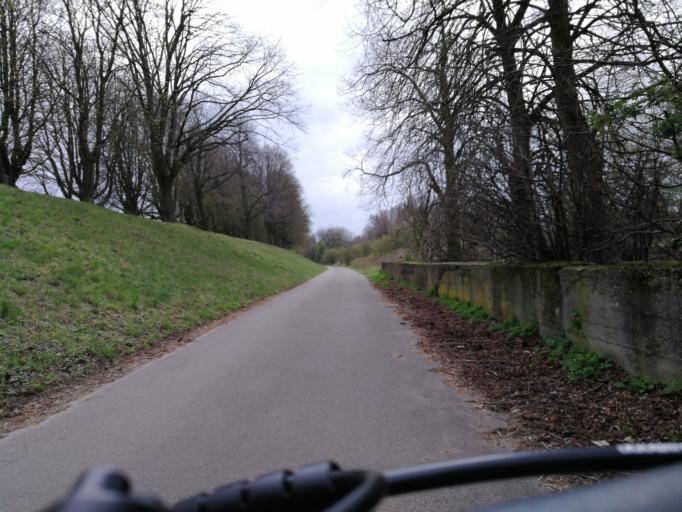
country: DE
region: North Rhine-Westphalia
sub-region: Regierungsbezirk Dusseldorf
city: Neuss
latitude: 51.1923
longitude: 6.7258
